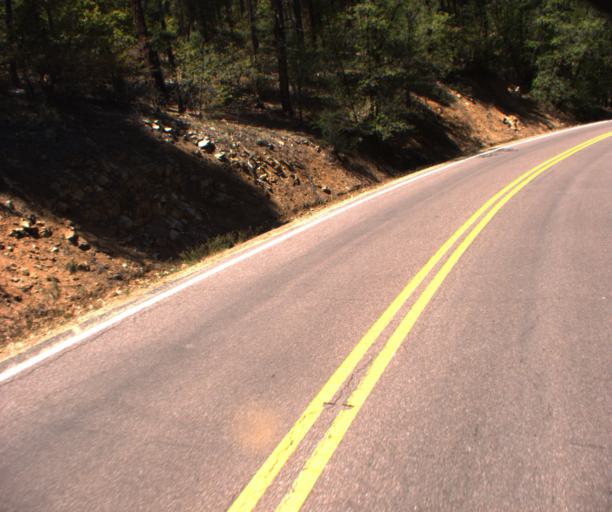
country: US
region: Arizona
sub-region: Yavapai County
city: Prescott
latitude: 34.4826
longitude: -112.5033
